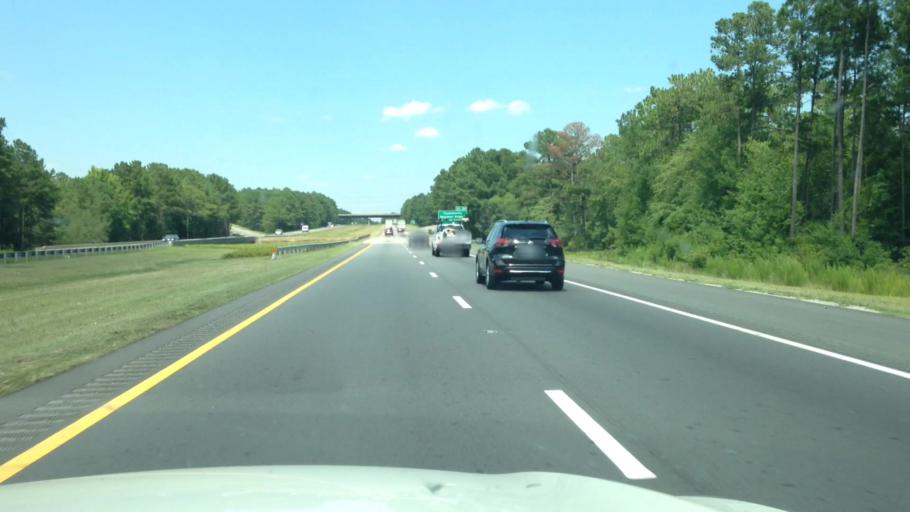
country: US
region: North Carolina
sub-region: Cumberland County
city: Hope Mills
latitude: 34.9570
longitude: -78.8949
